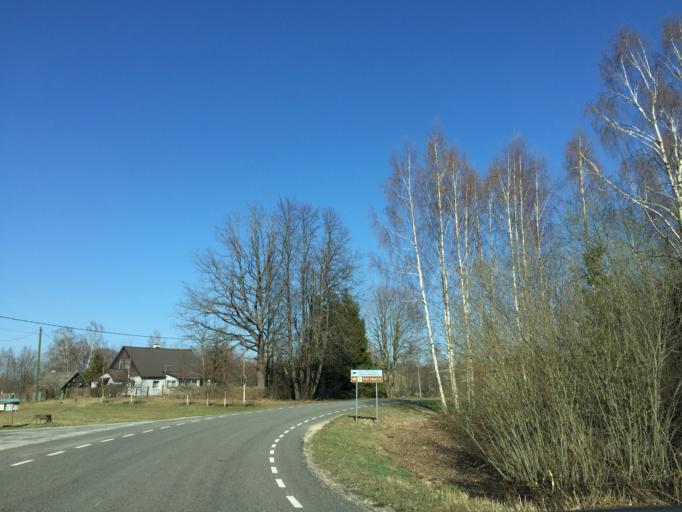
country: EE
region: Viljandimaa
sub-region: Viiratsi vald
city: Viiratsi
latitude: 58.2776
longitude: 25.6866
